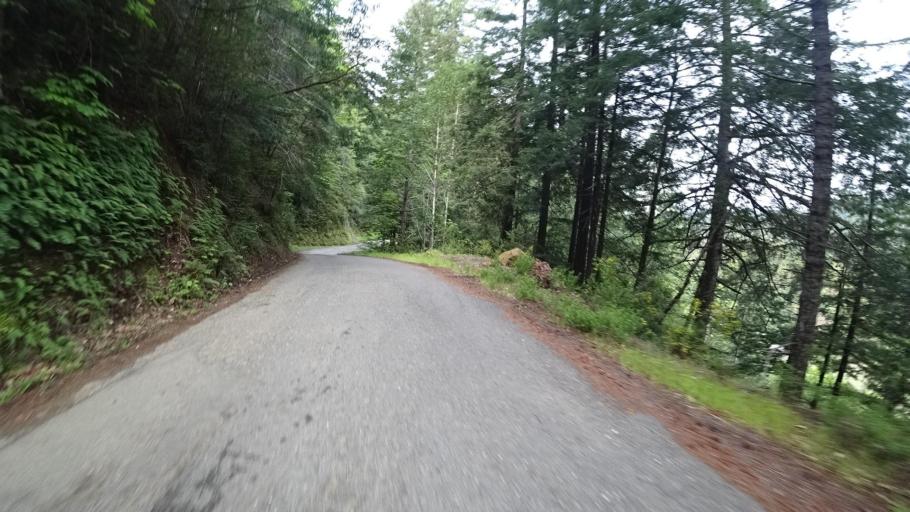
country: US
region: California
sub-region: Humboldt County
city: Redway
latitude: 40.3385
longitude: -123.8621
